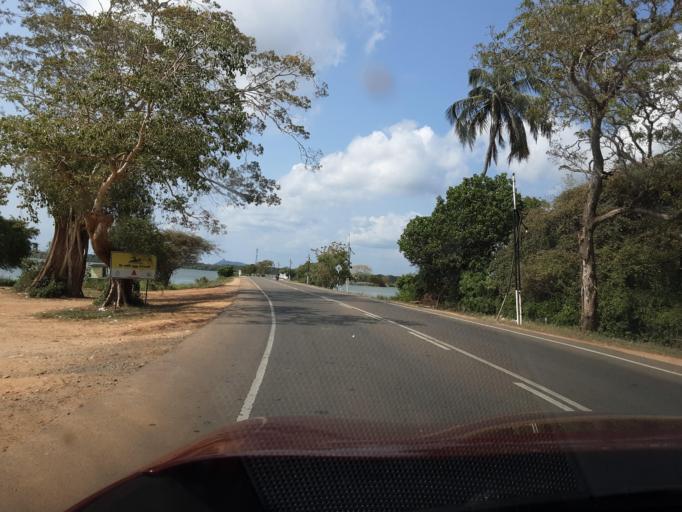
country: LK
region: Southern
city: Tangalla
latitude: 6.2844
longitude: 81.2316
